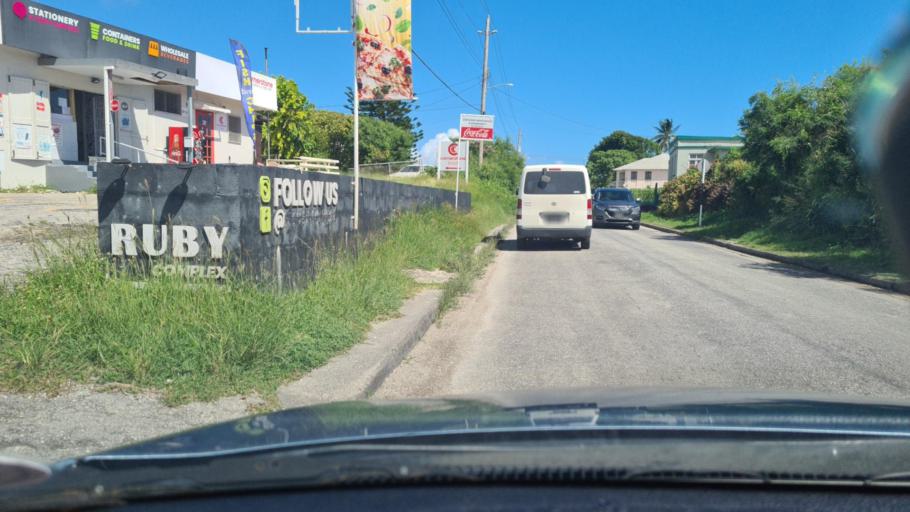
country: BB
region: Saint Philip
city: Crane
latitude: 13.1249
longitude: -59.4499
